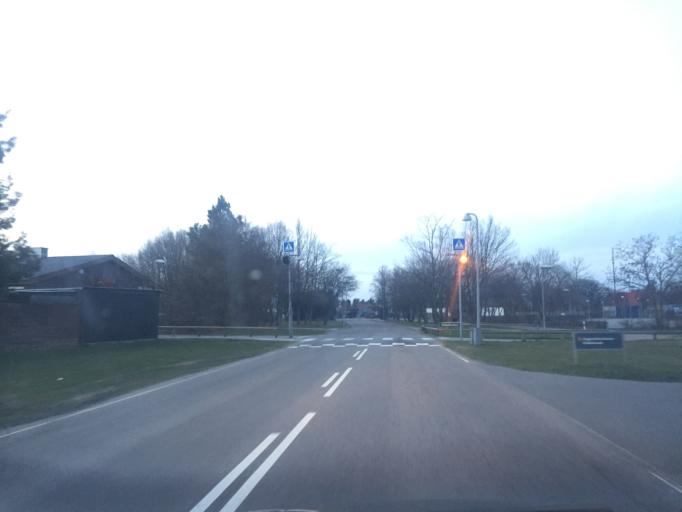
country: DK
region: Capital Region
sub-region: Hoje-Taastrup Kommune
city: Taastrup
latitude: 55.6416
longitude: 12.3089
